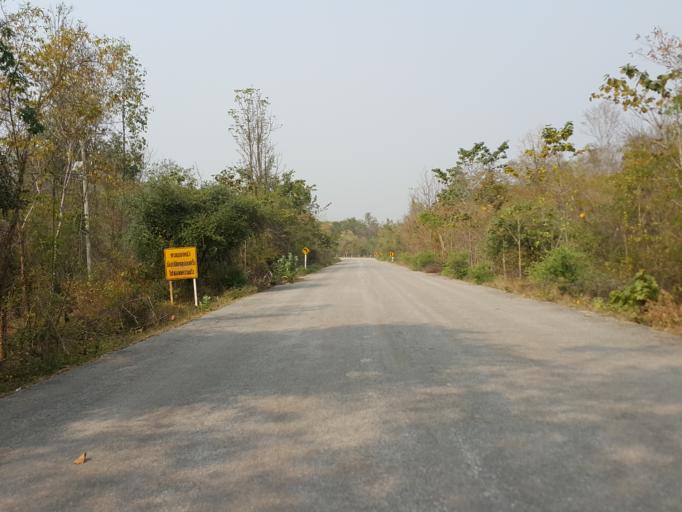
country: TH
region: Lampang
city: Mae Phrik
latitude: 17.5014
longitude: 99.0832
